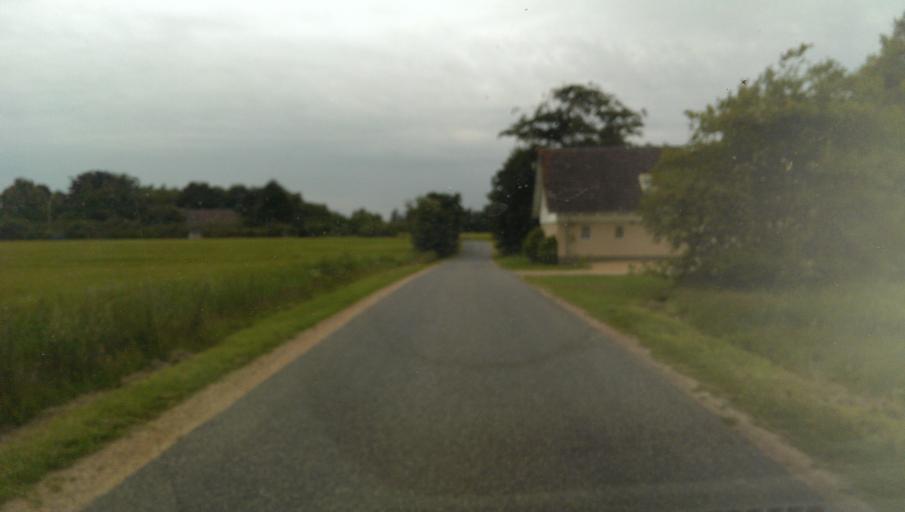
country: DK
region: South Denmark
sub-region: Esbjerg Kommune
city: Bramming
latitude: 55.4791
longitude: 8.7180
